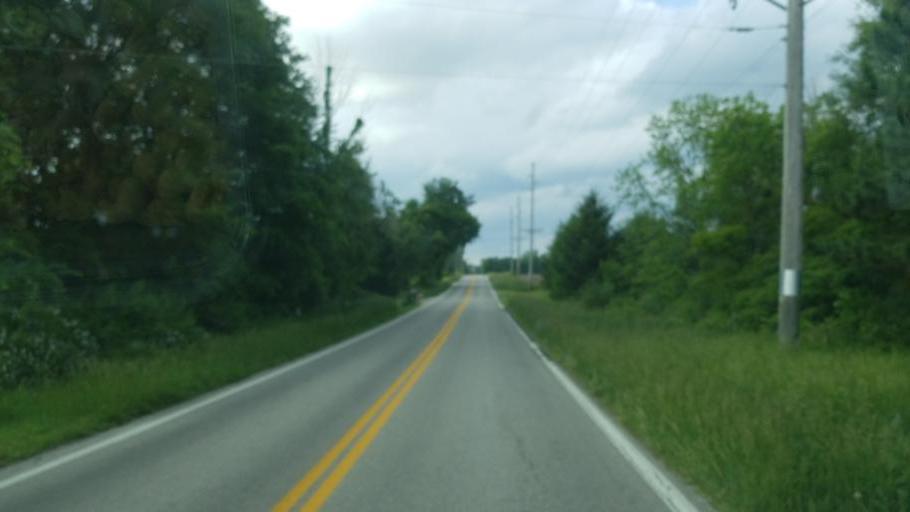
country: US
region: Ohio
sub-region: Knox County
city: Centerburg
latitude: 40.2968
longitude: -82.7850
